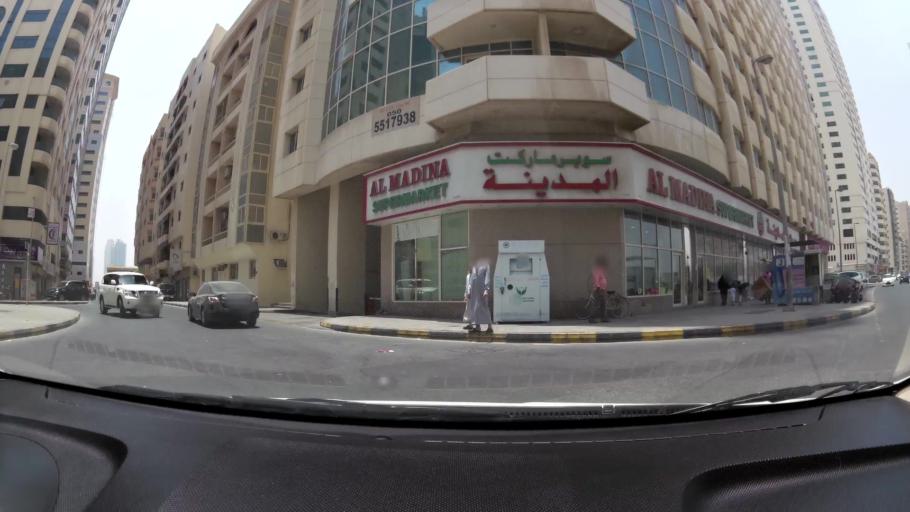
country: AE
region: Ash Shariqah
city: Sharjah
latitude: 25.3283
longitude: 55.3767
